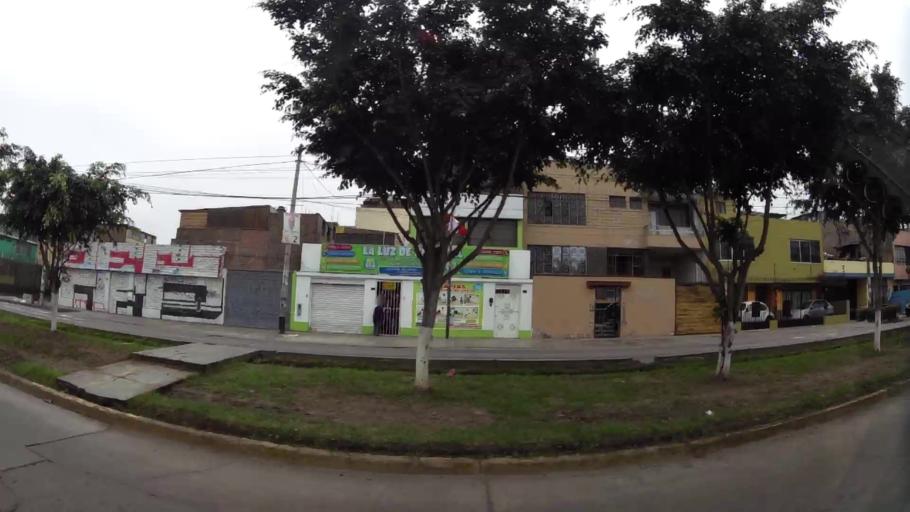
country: PE
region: Lima
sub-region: Lima
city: San Luis
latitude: -12.0844
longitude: -77.0192
